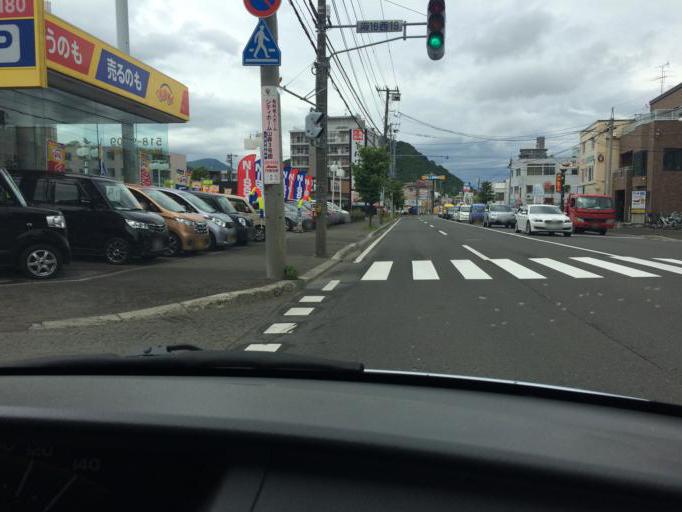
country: JP
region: Hokkaido
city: Sapporo
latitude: 43.0364
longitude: 141.3317
